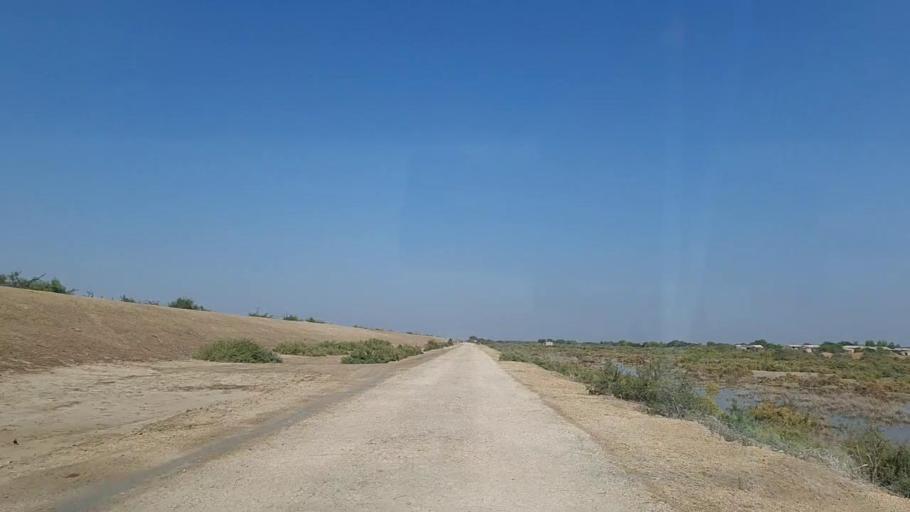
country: PK
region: Sindh
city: Chuhar Jamali
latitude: 24.4568
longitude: 68.0004
